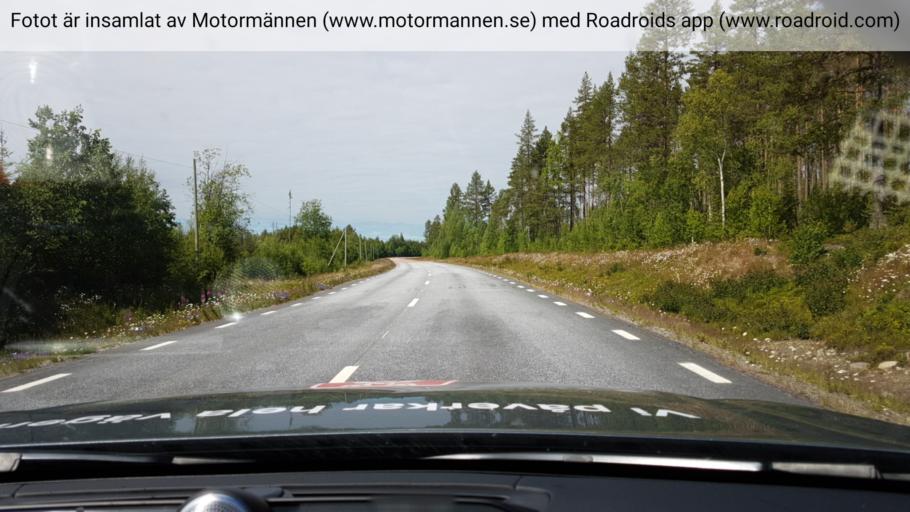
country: SE
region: Vaesterbotten
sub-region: Dorotea Kommun
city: Dorotea
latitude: 64.1946
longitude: 16.2982
